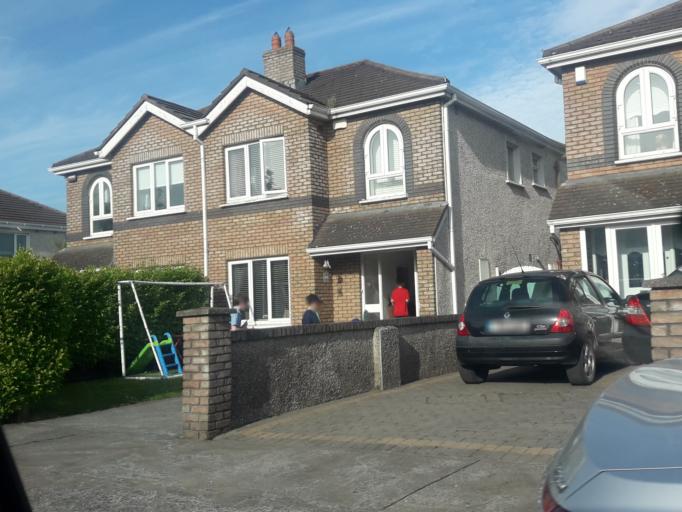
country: IE
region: Leinster
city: Hartstown
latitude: 53.3868
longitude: -6.4156
